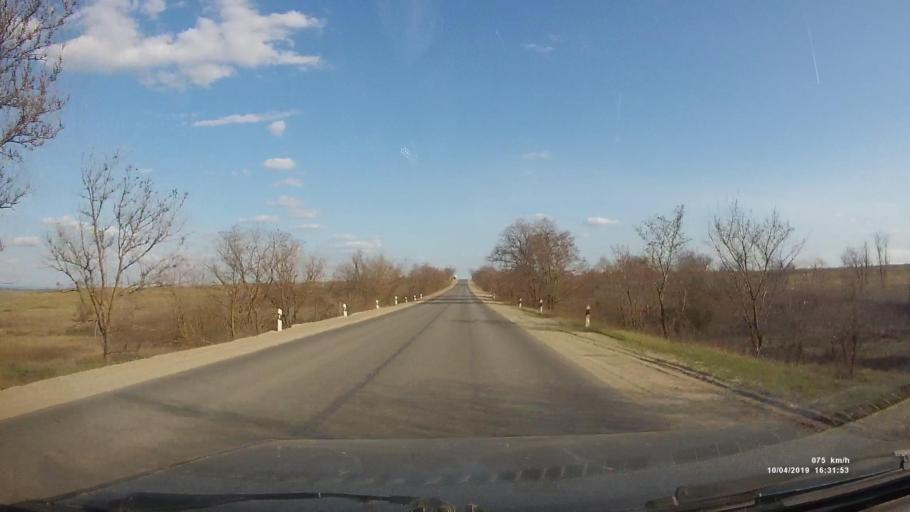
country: RU
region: Rostov
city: Staraya Stanitsa
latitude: 48.2507
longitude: 40.3808
